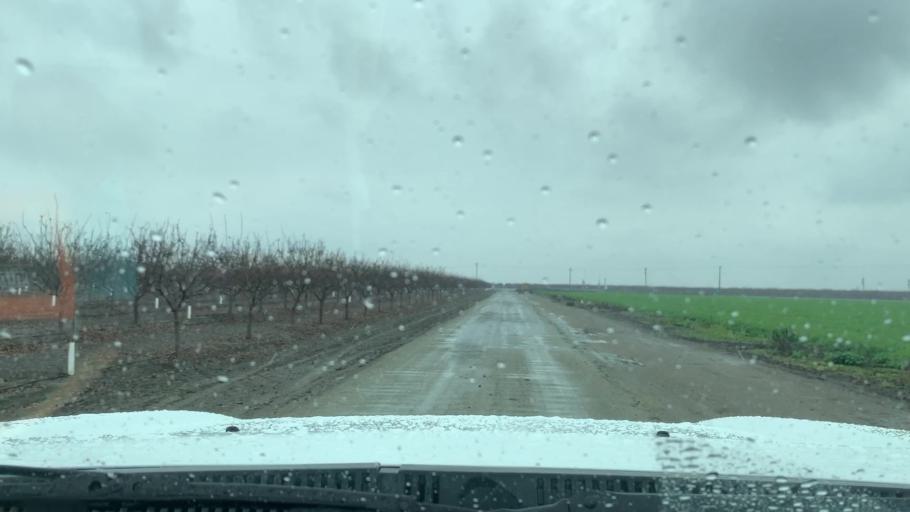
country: US
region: California
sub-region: Kings County
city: Corcoran
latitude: 36.0254
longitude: -119.5005
